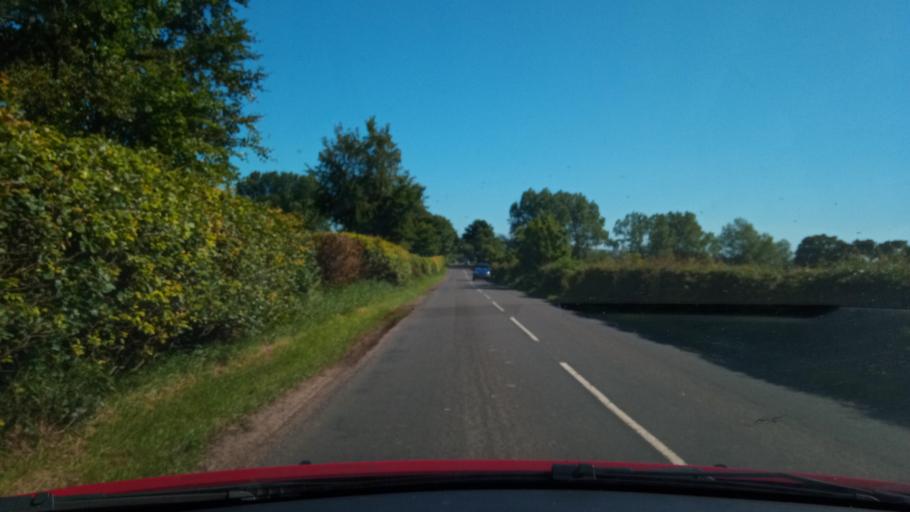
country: GB
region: Scotland
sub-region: East Lothian
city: East Linton
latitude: 55.9999
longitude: -2.6231
